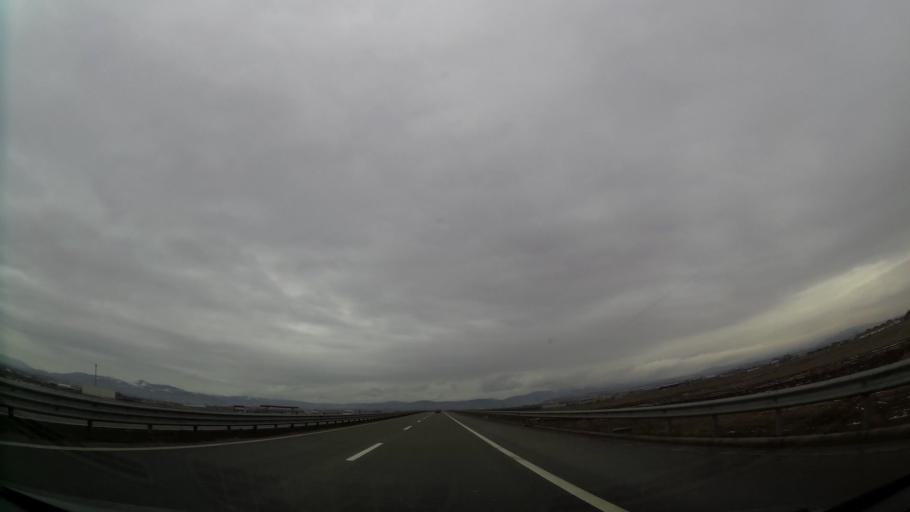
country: XK
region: Pristina
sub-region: Lipjan
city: Lipljan
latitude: 42.5306
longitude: 21.1534
